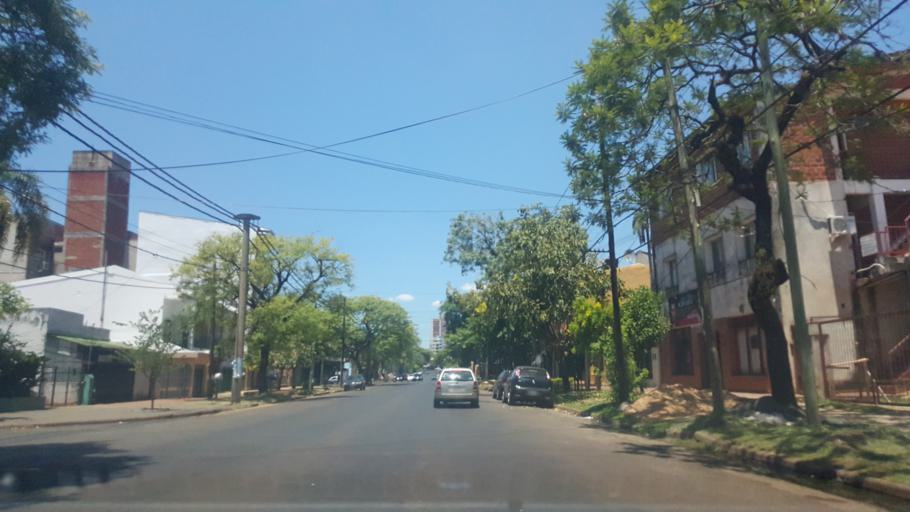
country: AR
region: Misiones
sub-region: Departamento de Capital
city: Posadas
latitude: -27.3667
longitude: -55.9064
